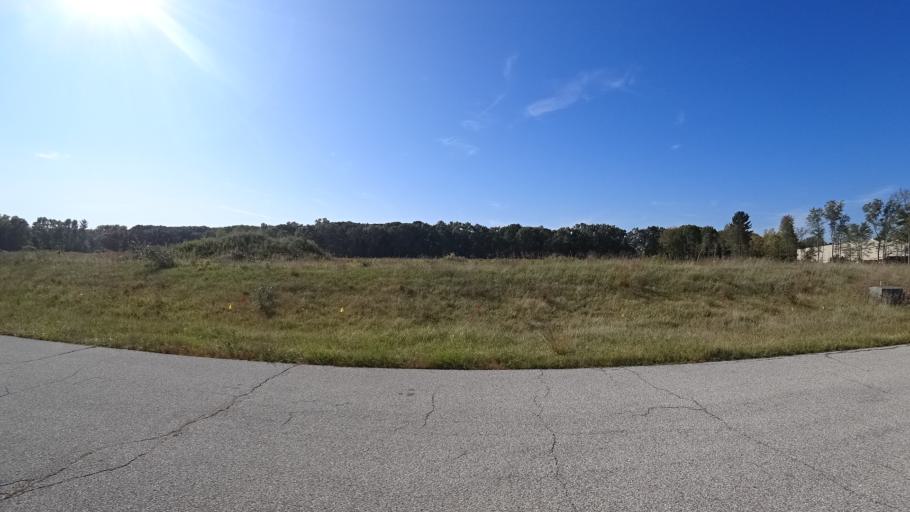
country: US
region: Indiana
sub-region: LaPorte County
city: Trail Creek
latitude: 41.6972
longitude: -86.8420
